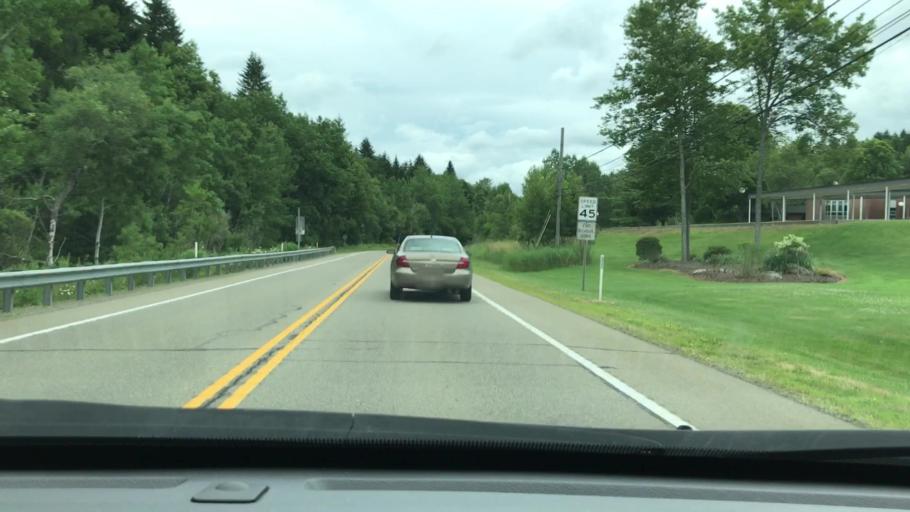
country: US
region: Pennsylvania
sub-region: Elk County
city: Johnsonburg
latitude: 41.5157
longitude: -78.6795
